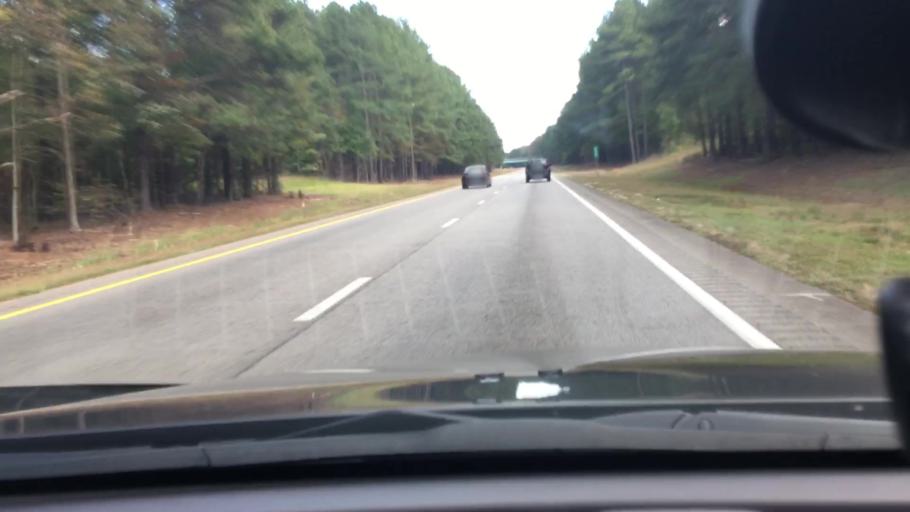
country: US
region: North Carolina
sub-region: Nash County
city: Spring Hope
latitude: 35.7911
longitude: -78.1456
